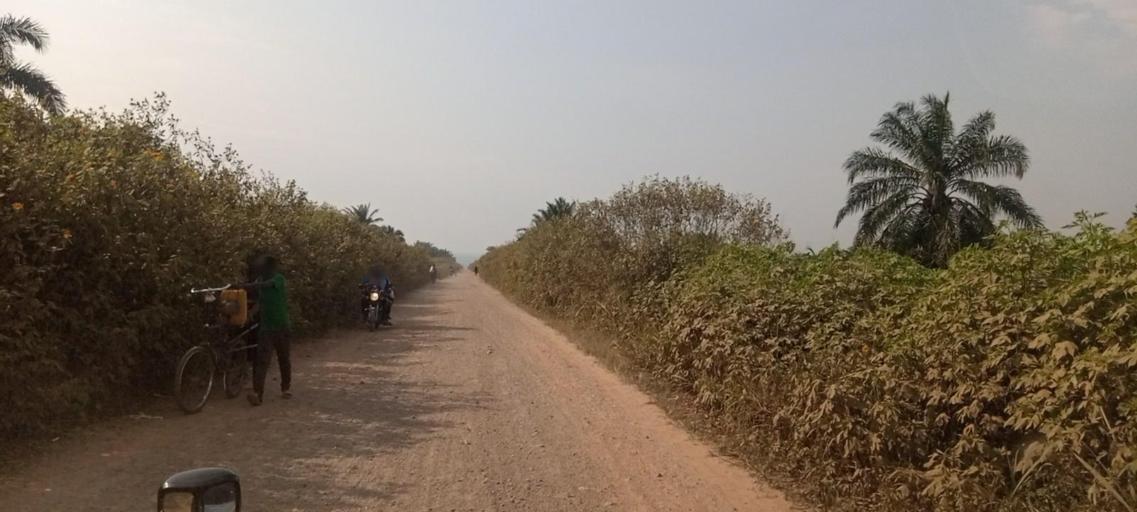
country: CD
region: Kasai-Oriental
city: Mbuji-Mayi
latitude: -6.3634
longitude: 23.8186
